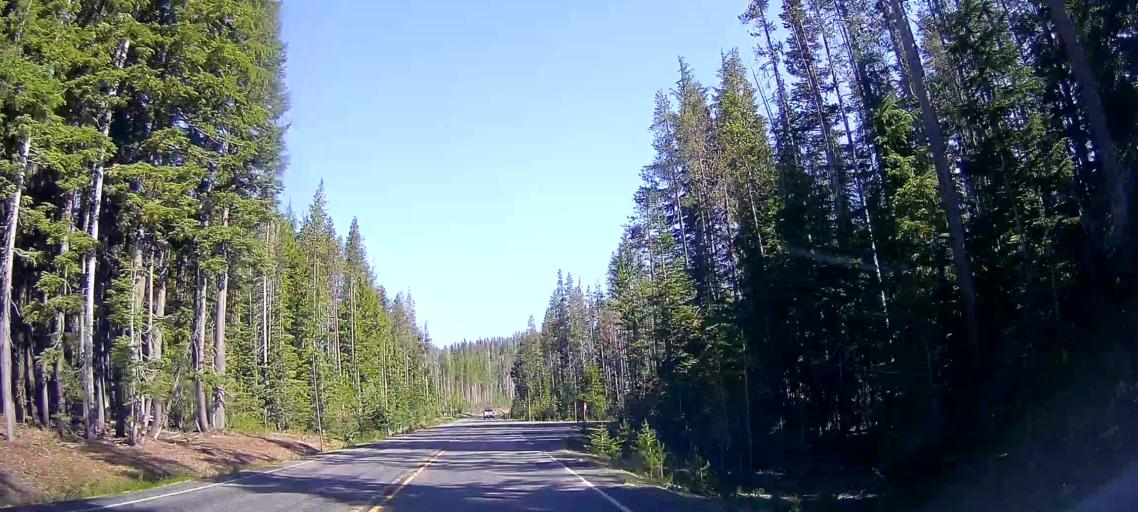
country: US
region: Oregon
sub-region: Jackson County
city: Shady Cove
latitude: 42.8392
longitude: -122.1453
